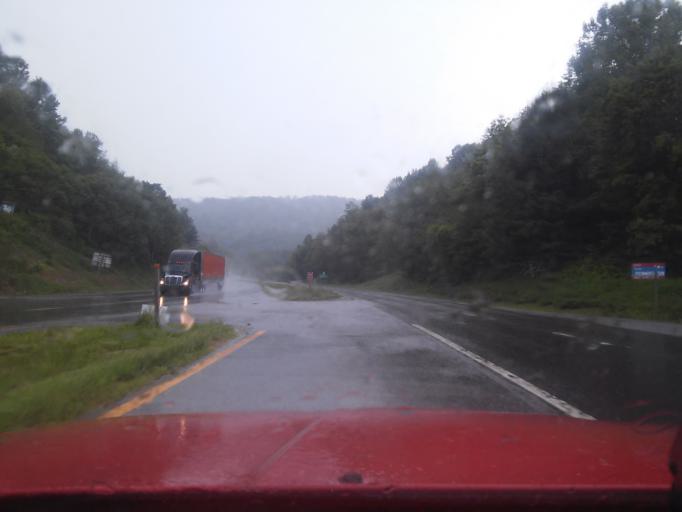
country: US
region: Virginia
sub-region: Montgomery County
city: Prices Fork
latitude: 37.2900
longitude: -80.4991
